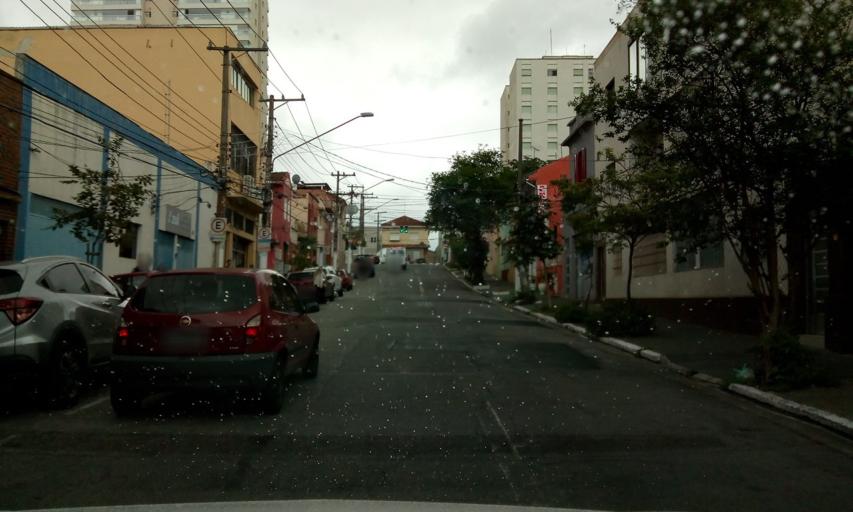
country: BR
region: Sao Paulo
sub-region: Sao Paulo
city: Sao Paulo
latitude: -23.5644
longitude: -46.6215
